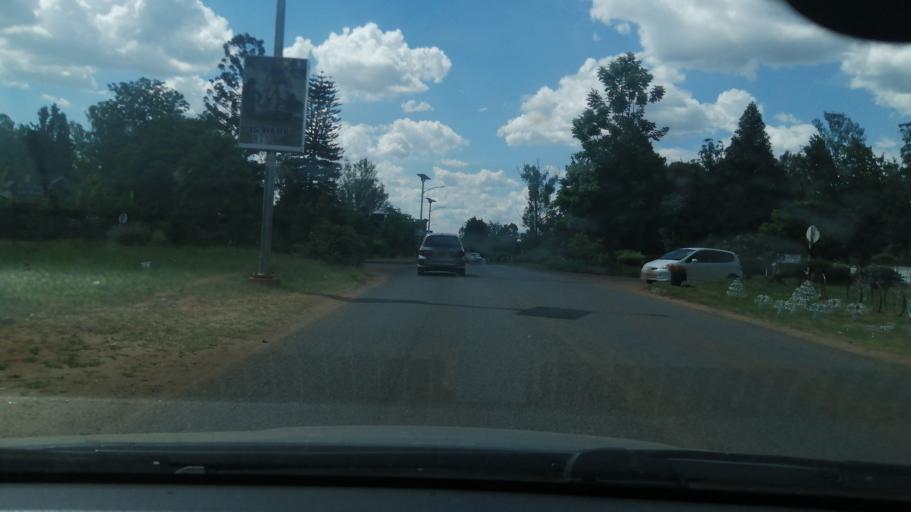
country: ZW
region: Harare
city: Harare
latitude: -17.7931
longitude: 31.0671
